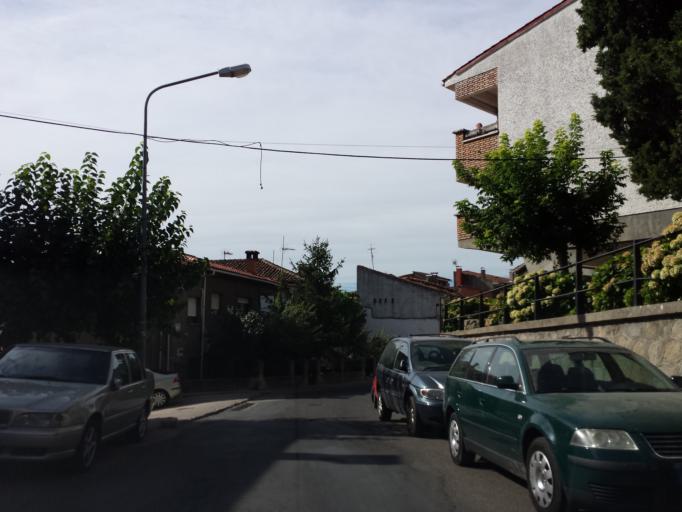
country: ES
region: Castille and Leon
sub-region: Provincia de Avila
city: Piedralaves
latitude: 40.3191
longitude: -4.6980
